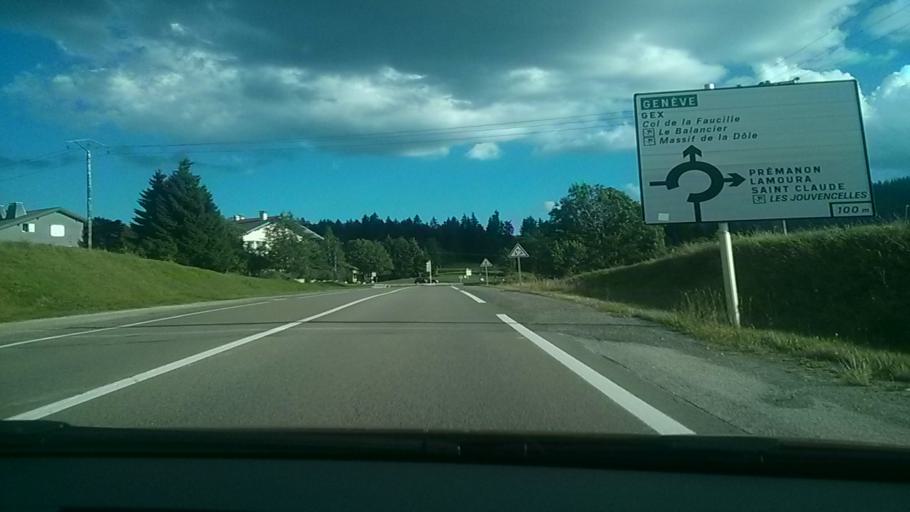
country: FR
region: Franche-Comte
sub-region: Departement du Jura
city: Les Rousses
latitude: 46.4642
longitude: 6.0715
